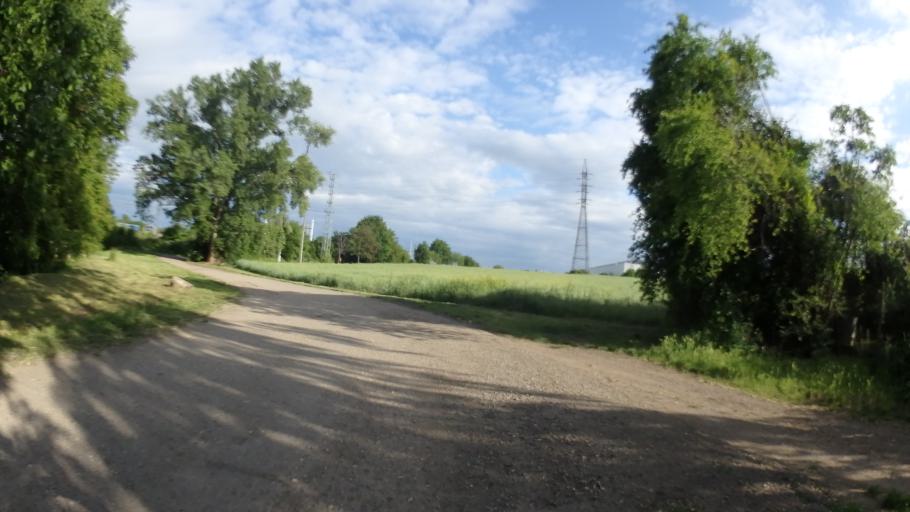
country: CZ
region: South Moravian
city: Moravany
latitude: 49.1587
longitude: 16.6058
